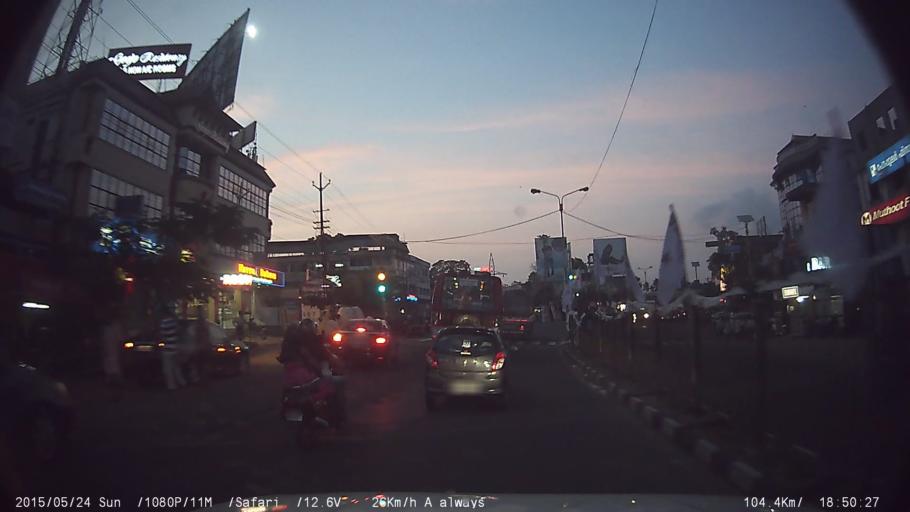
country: IN
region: Kerala
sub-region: Ernakulam
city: Aluva
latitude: 10.1551
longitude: 76.3544
